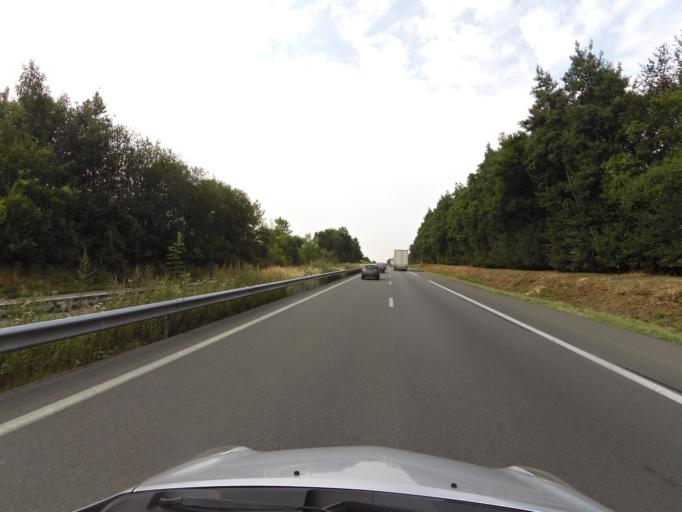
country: FR
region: Picardie
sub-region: Departement de l'Aisne
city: Holnon
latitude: 49.9212
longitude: 3.2304
